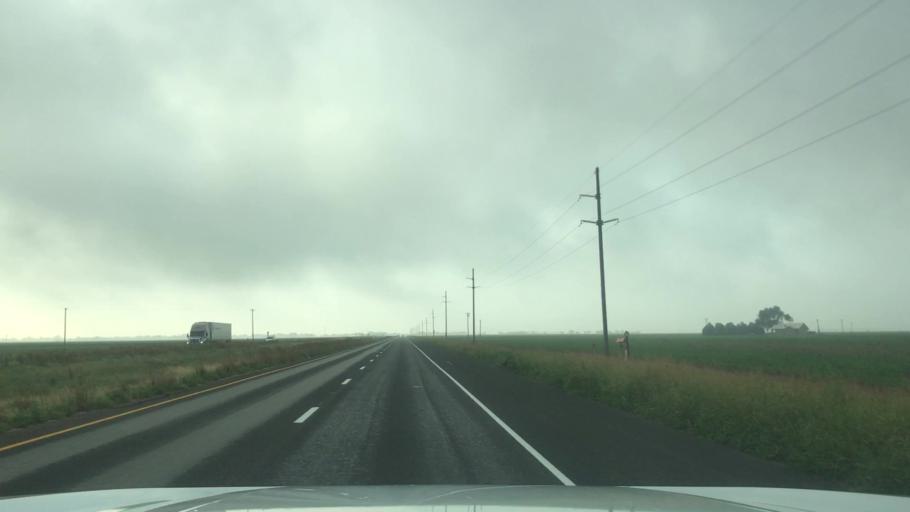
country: US
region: Texas
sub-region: Lubbock County
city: Slaton
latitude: 33.3735
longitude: -101.5758
